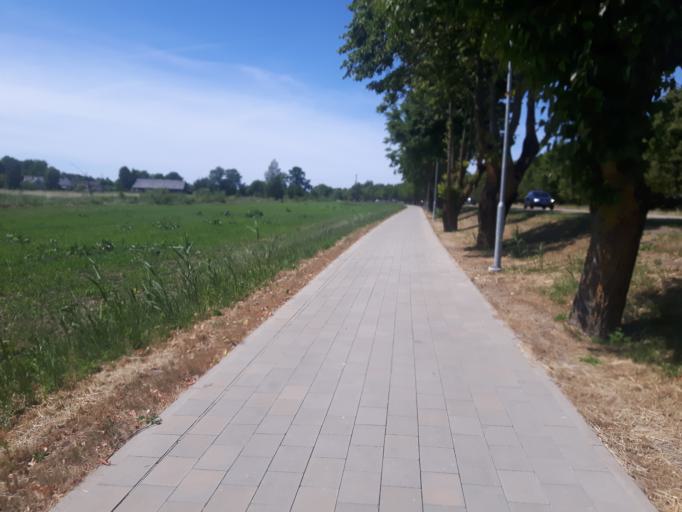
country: LV
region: Grobina
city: Grobina
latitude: 56.5333
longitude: 21.1080
